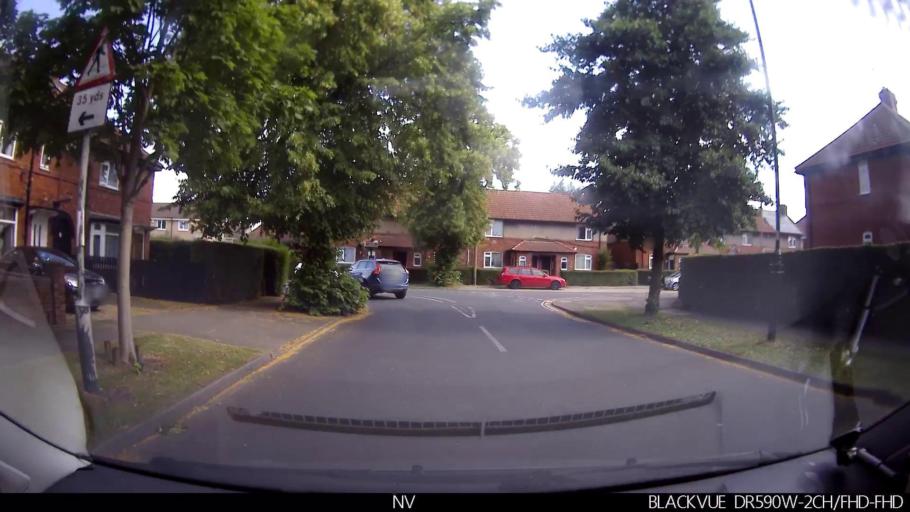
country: GB
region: England
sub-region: City of York
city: York
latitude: 53.9723
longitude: -1.0696
